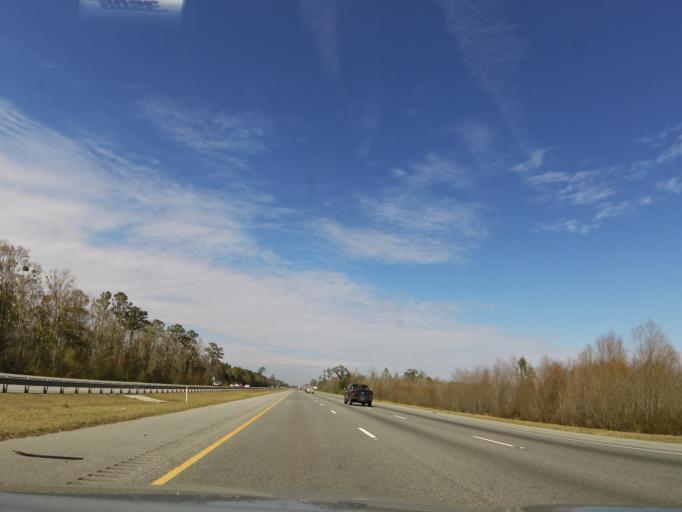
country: US
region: Georgia
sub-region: McIntosh County
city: Darien
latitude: 31.4449
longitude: -81.4448
